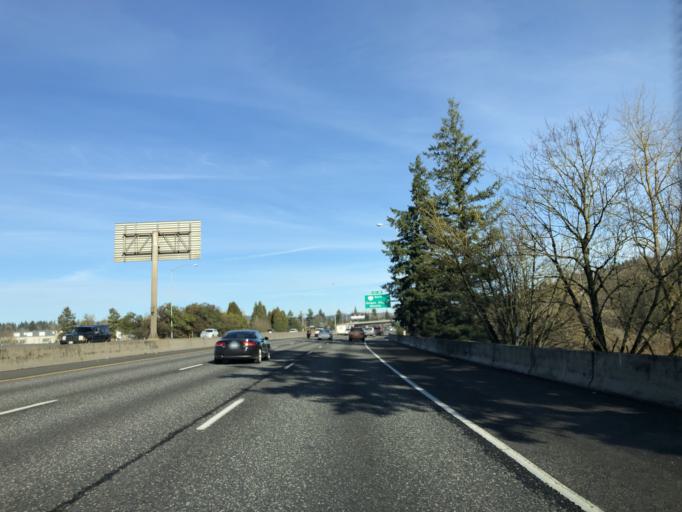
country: US
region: Oregon
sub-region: Clackamas County
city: Gladstone
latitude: 45.3713
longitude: -122.5917
